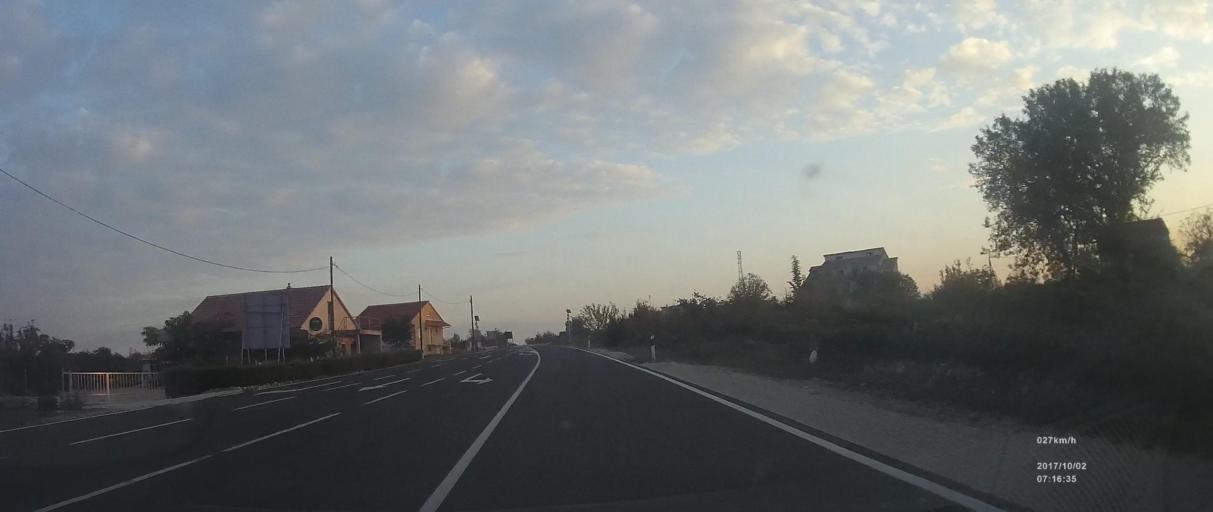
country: HR
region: Zadarska
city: Benkovac
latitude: 44.0001
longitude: 15.5877
